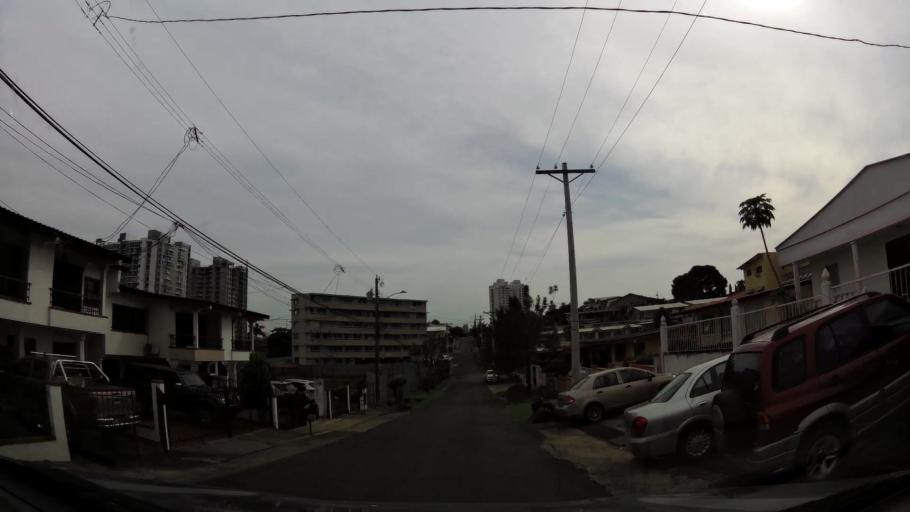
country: PA
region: Panama
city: Panama
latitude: 9.0141
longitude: -79.5185
